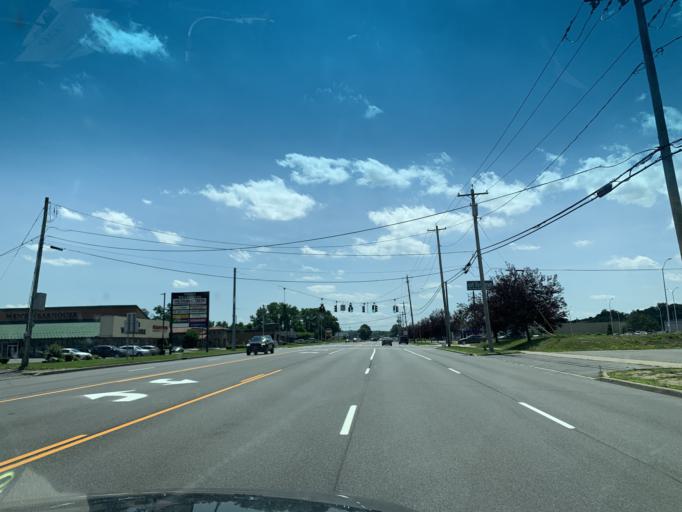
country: US
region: New York
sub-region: Oneida County
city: New York Mills
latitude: 43.0891
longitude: -75.3117
